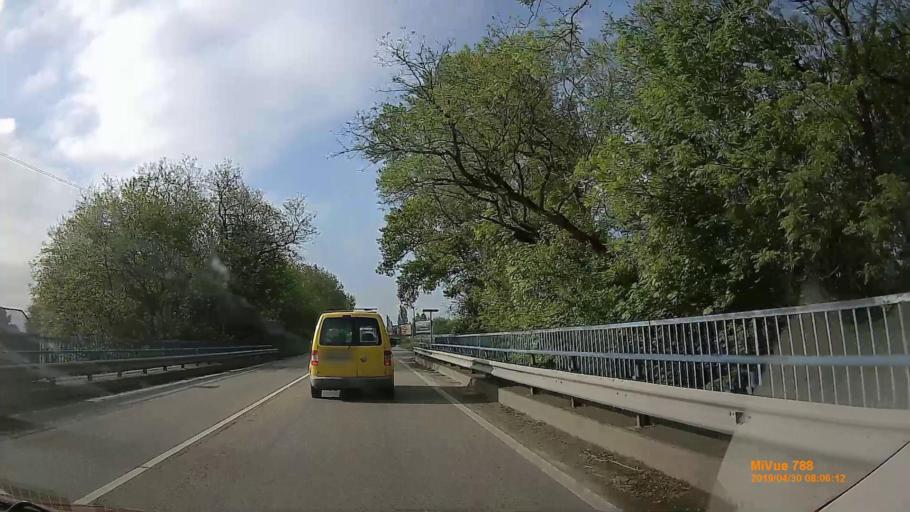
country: HU
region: Pest
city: Vac
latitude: 47.8098
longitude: 19.0942
